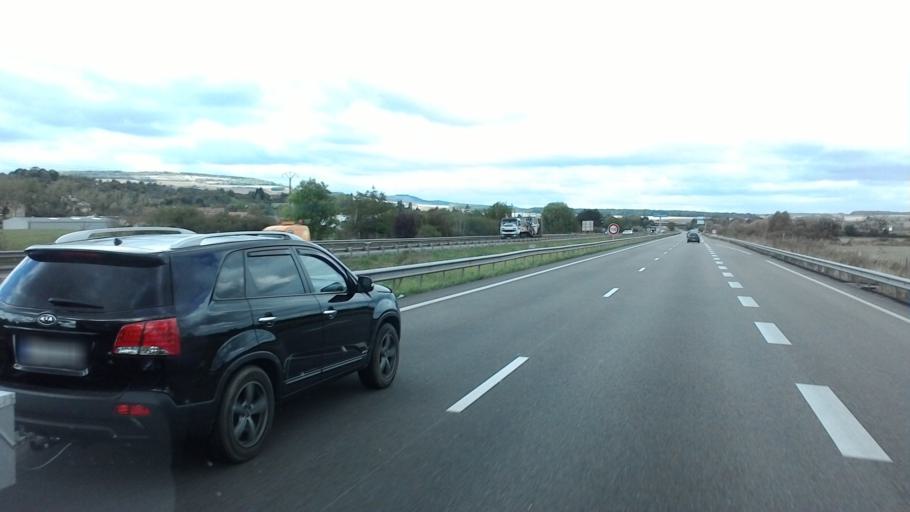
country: FR
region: Lorraine
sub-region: Departement de Meurthe-et-Moselle
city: Pont-a-Mousson
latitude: 48.9289
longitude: 6.1110
